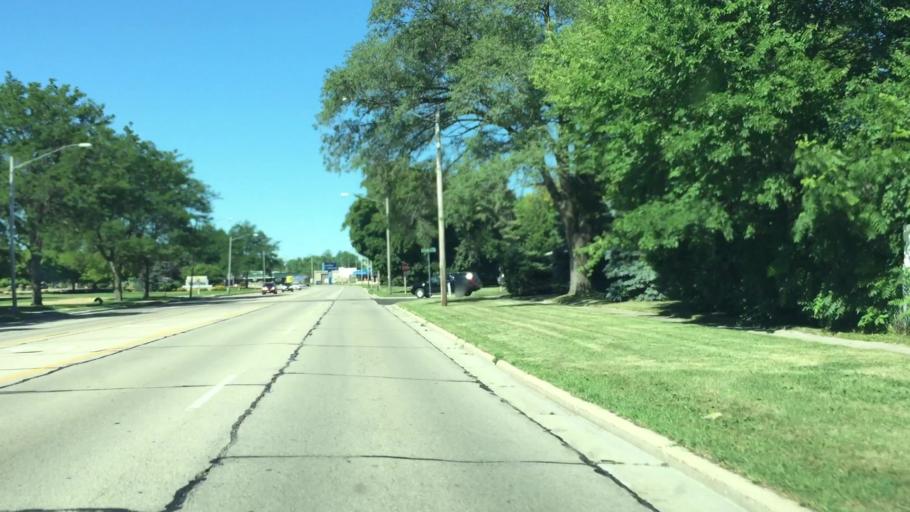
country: US
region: Wisconsin
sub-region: Outagamie County
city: Appleton
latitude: 44.2401
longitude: -88.4210
